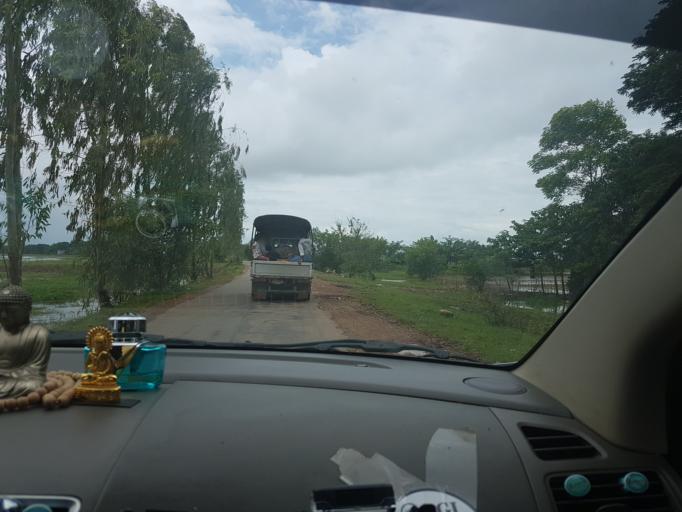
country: MM
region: Bago
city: Nyaunglebin
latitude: 17.9172
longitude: 96.8286
